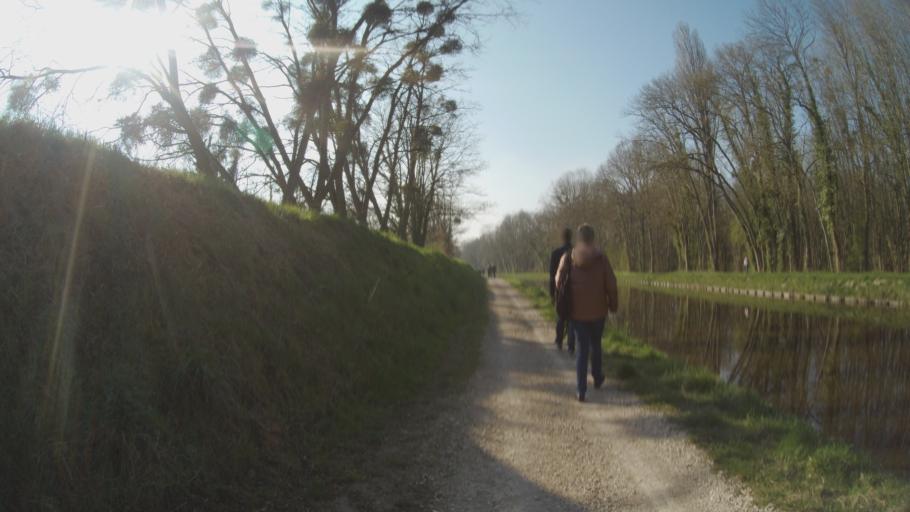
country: FR
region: Centre
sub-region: Departement du Loiret
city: Checy
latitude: 47.8933
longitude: 2.0108
